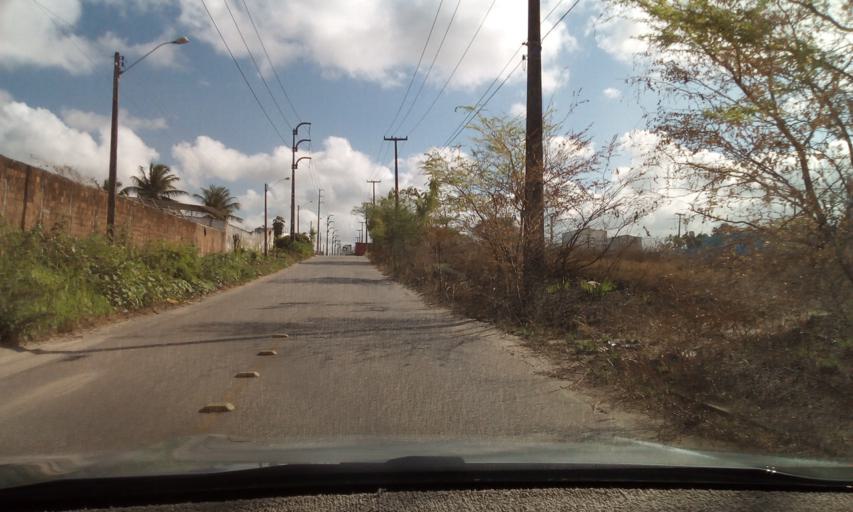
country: BR
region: Paraiba
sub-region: Bayeux
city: Bayeux
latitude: -7.1703
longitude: -34.9060
